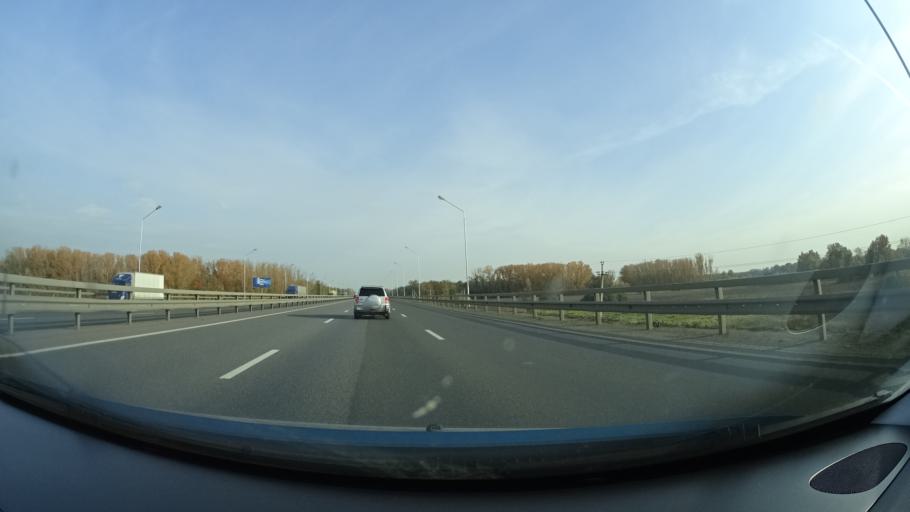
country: RU
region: Bashkortostan
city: Ufa
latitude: 54.6564
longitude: 55.8941
